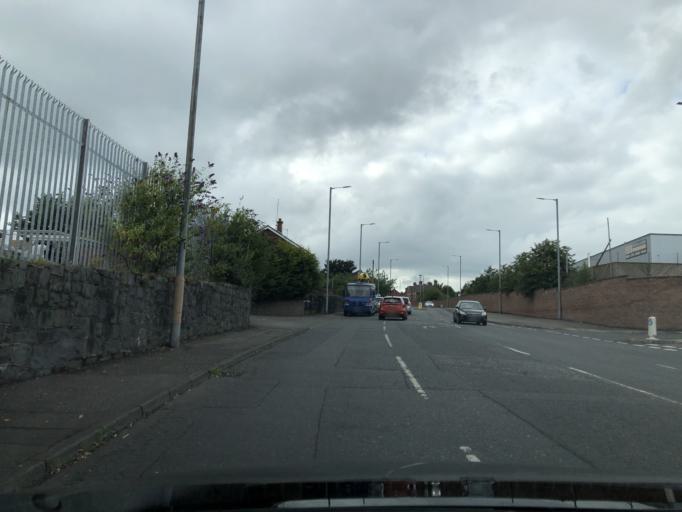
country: GB
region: Northern Ireland
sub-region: Newtownabbey District
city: Newtownabbey
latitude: 54.6519
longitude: -5.9184
